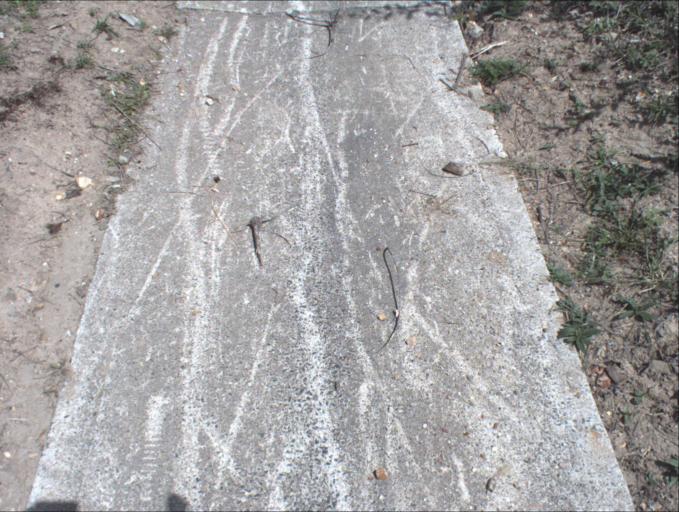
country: AU
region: Queensland
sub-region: Logan
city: Waterford West
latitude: -27.7036
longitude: 153.1631
